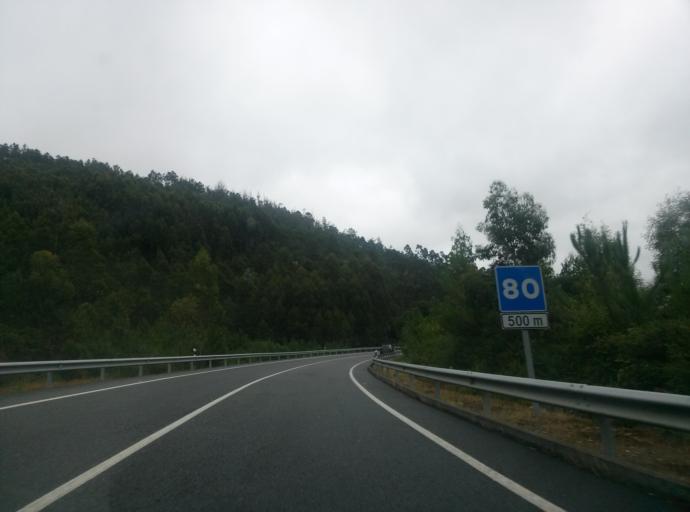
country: ES
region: Galicia
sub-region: Provincia de Lugo
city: Viveiro
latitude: 43.5696
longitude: -7.6429
